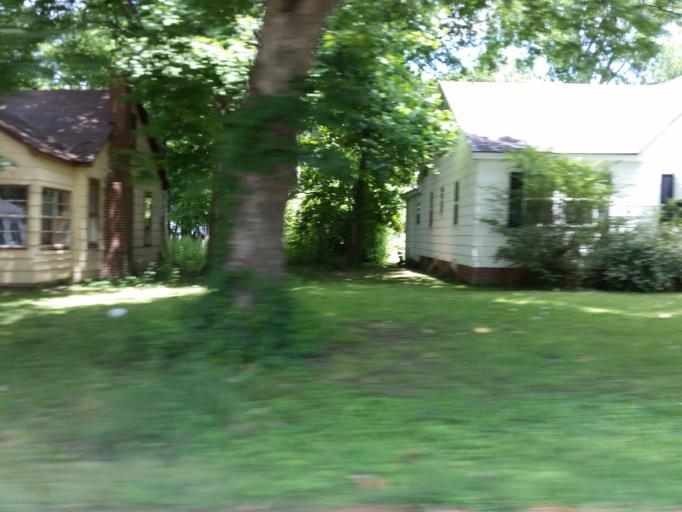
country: US
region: Tennessee
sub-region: Lake County
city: Tiptonville
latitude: 36.3750
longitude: -89.4811
